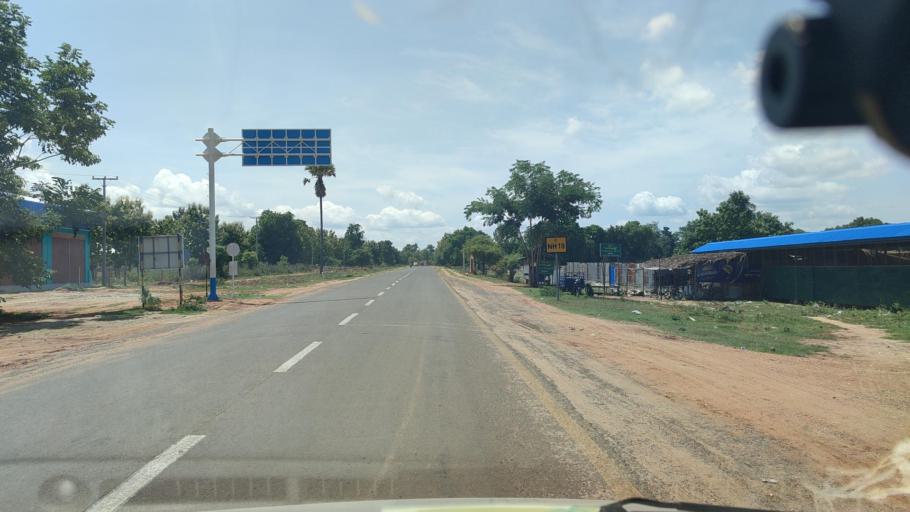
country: MM
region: Magway
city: Magway
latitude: 20.1957
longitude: 95.0139
